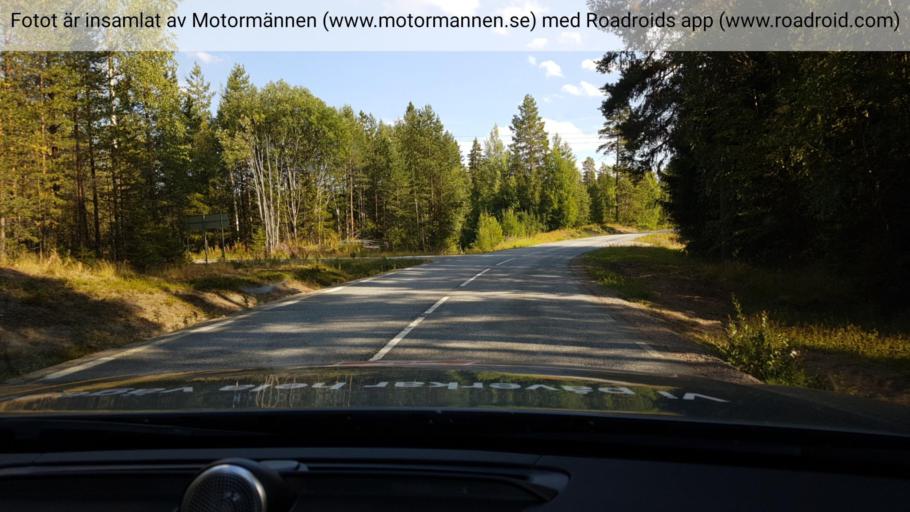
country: SE
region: Vaesterbotten
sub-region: Dorotea Kommun
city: Dorotea
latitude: 63.9009
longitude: 16.3590
